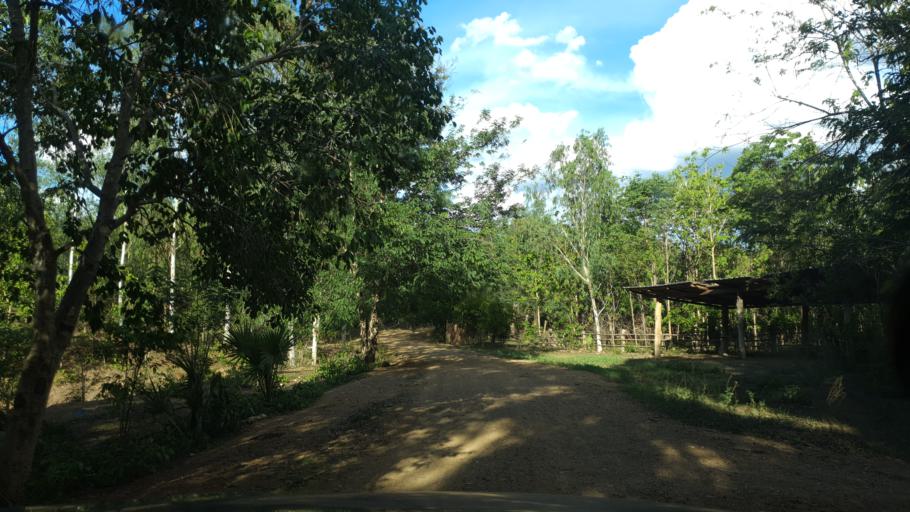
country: TH
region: Lampang
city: Sop Prap
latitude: 17.8823
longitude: 99.2939
